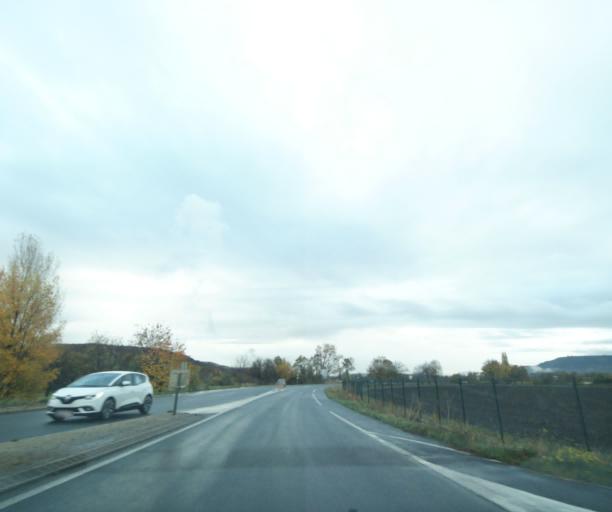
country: FR
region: Auvergne
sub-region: Departement du Puy-de-Dome
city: Aulnat
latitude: 45.7787
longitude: 3.1475
